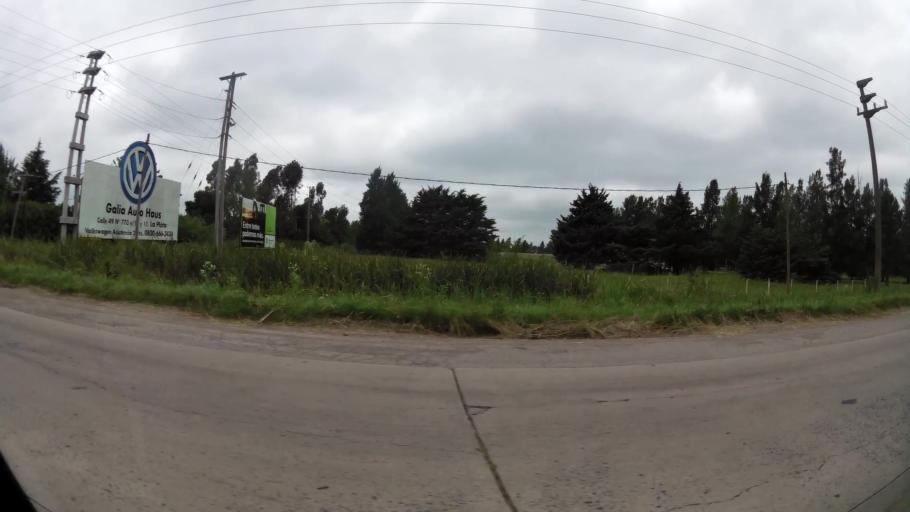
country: AR
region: Buenos Aires
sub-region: Partido de Brandsen
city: Brandsen
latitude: -35.0416
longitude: -58.0990
